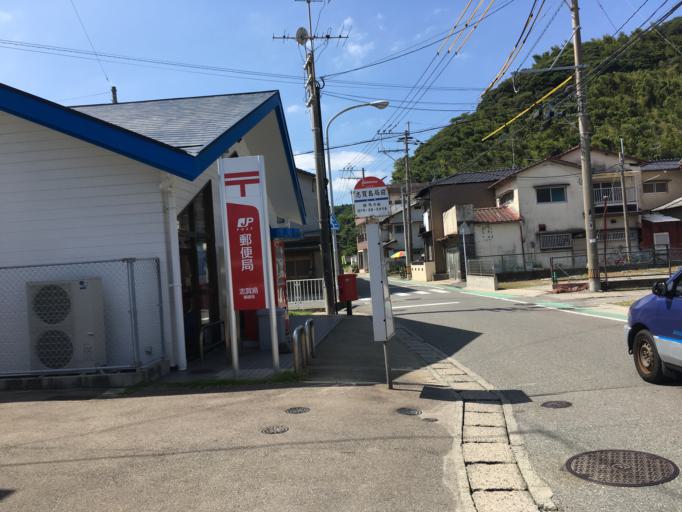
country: JP
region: Fukuoka
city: Fukuoka-shi
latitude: 33.6631
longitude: 130.3123
